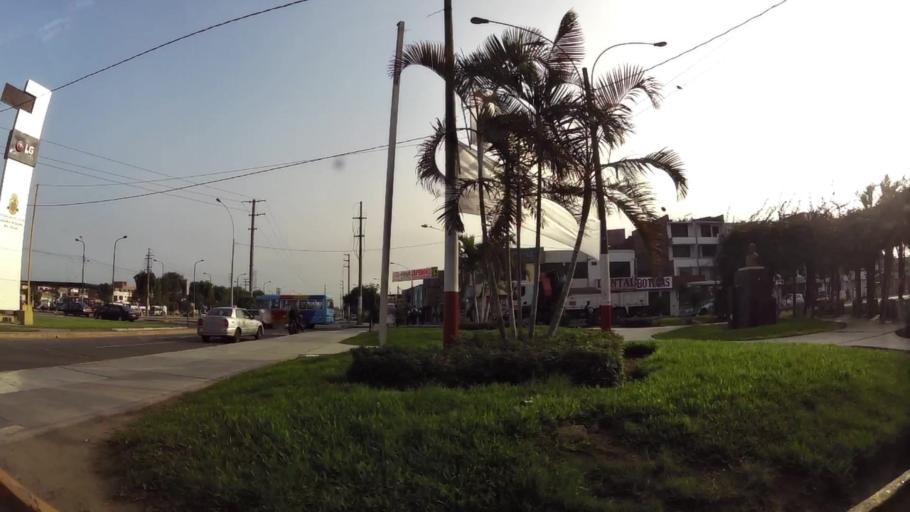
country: PE
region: Callao
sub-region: Callao
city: Callao
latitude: -12.0130
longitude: -77.0952
